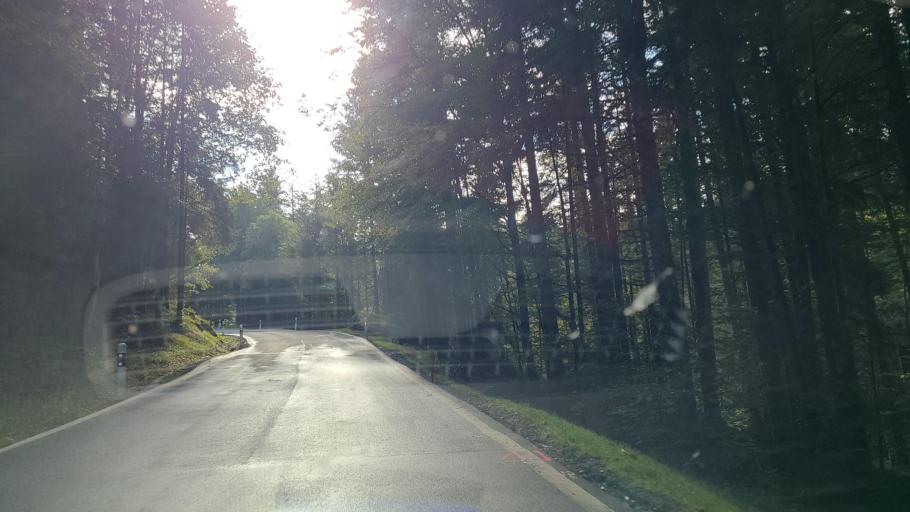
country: CH
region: Schwyz
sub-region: Bezirk March
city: Altendorf
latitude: 47.1313
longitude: 8.8245
